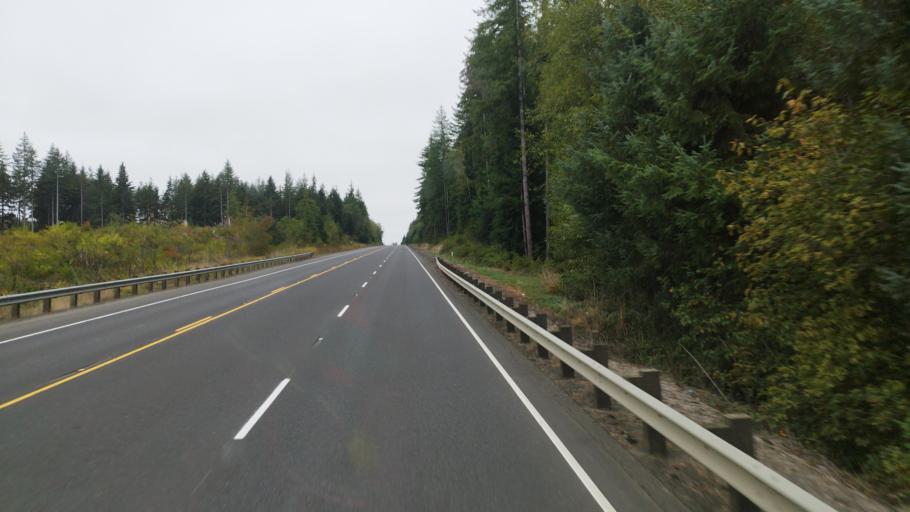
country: US
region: Washington
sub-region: Wahkiakum County
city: Cathlamet
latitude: 46.1746
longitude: -123.5416
